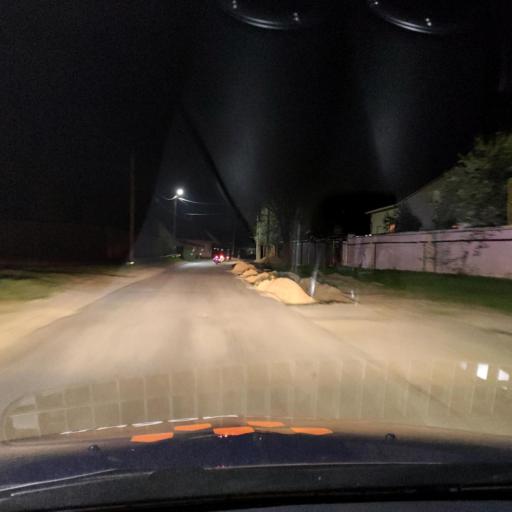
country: RU
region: Voronezj
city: Novaya Usman'
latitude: 51.6398
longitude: 39.3946
